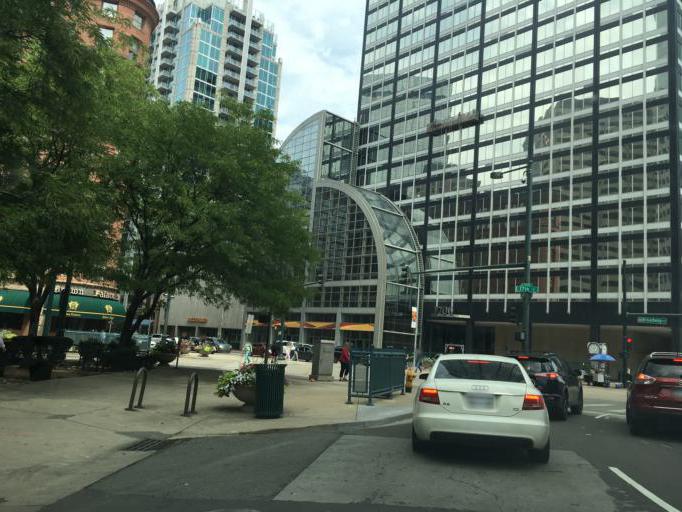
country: US
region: Colorado
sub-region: Denver County
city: Denver
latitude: 39.7432
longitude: -104.9879
